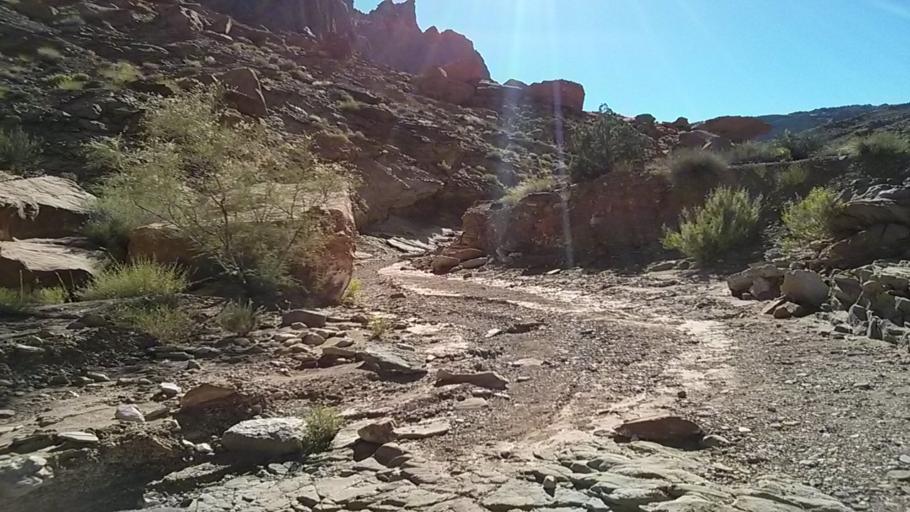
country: US
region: Utah
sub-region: Grand County
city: Moab
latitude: 38.4417
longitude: -109.9456
